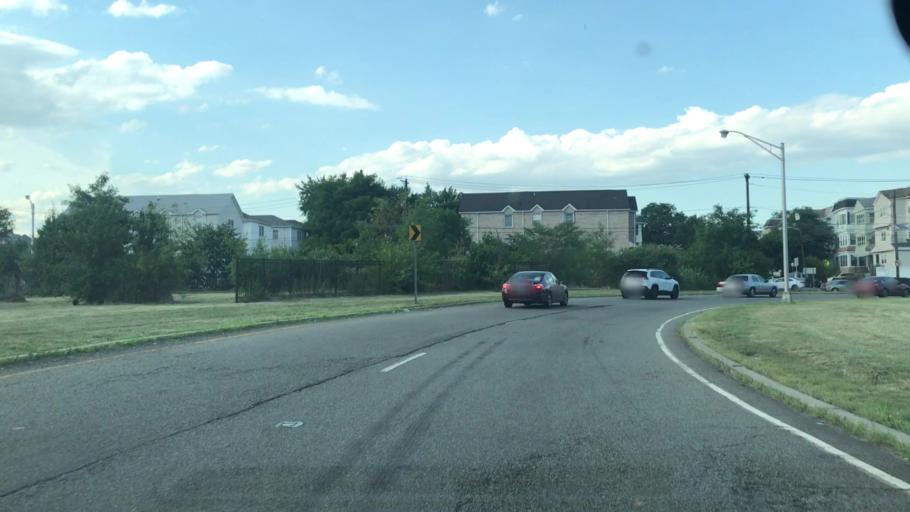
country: US
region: New Jersey
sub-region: Essex County
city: Newark
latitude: 40.7150
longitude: -74.1953
